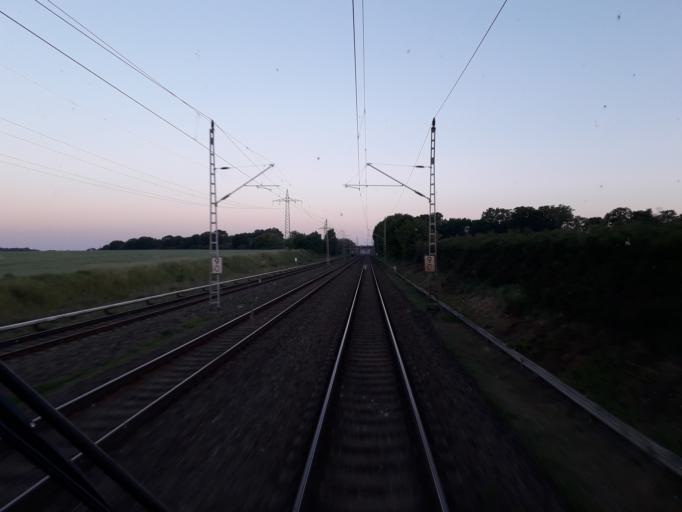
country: DE
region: Berlin
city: Blankenfelde
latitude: 52.6585
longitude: 13.3697
